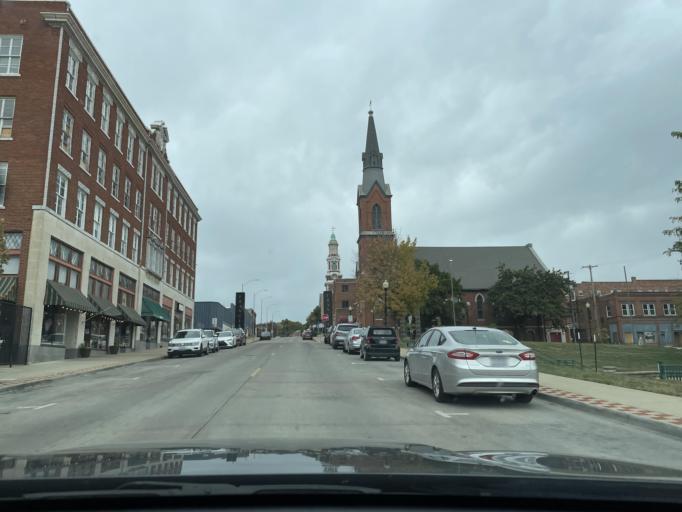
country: US
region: Missouri
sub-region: Buchanan County
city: Saint Joseph
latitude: 39.7668
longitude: -94.8518
